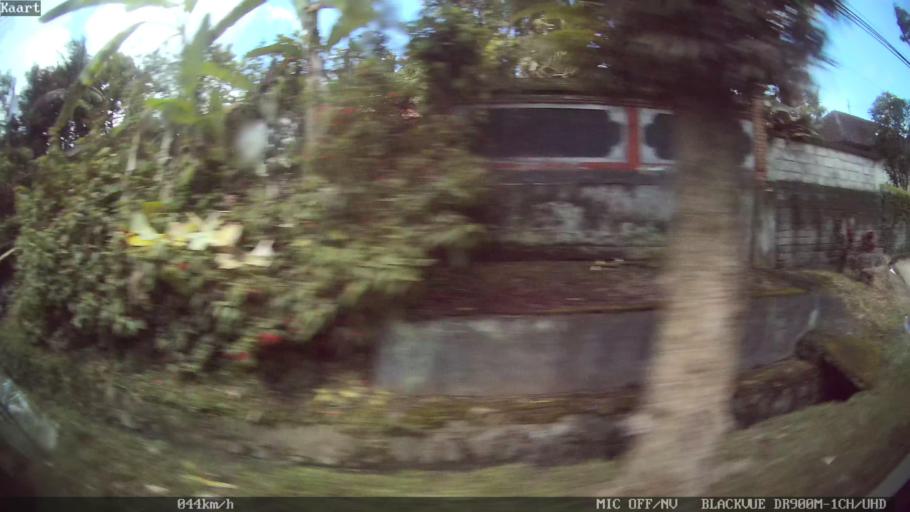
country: ID
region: Bali
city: Banjar Mulung
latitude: -8.5121
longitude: 115.3190
